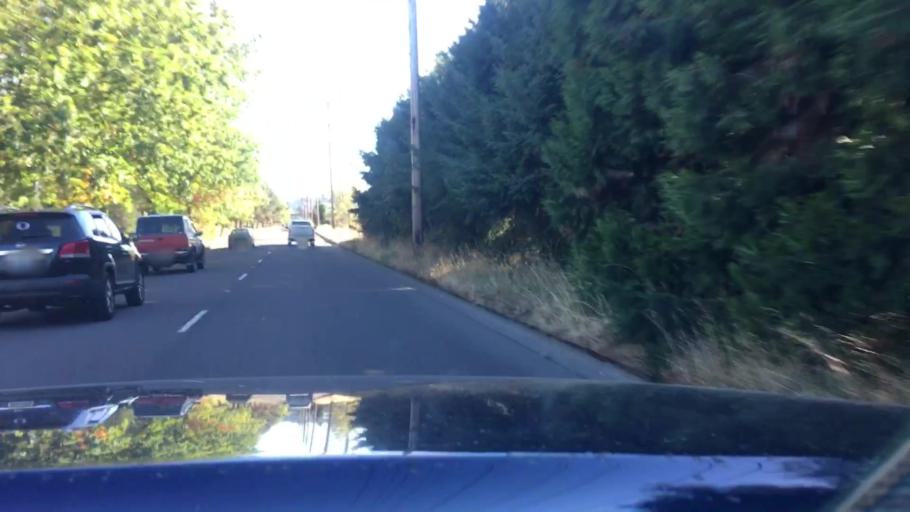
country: US
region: Oregon
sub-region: Lane County
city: Springfield
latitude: 44.0676
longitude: -123.0281
